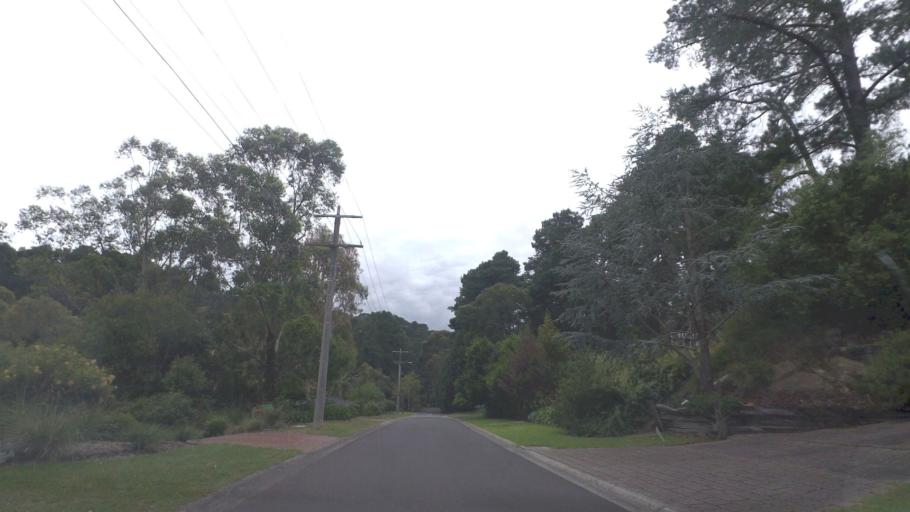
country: AU
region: Victoria
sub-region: Manningham
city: Park Orchards
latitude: -37.7883
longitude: 145.2124
